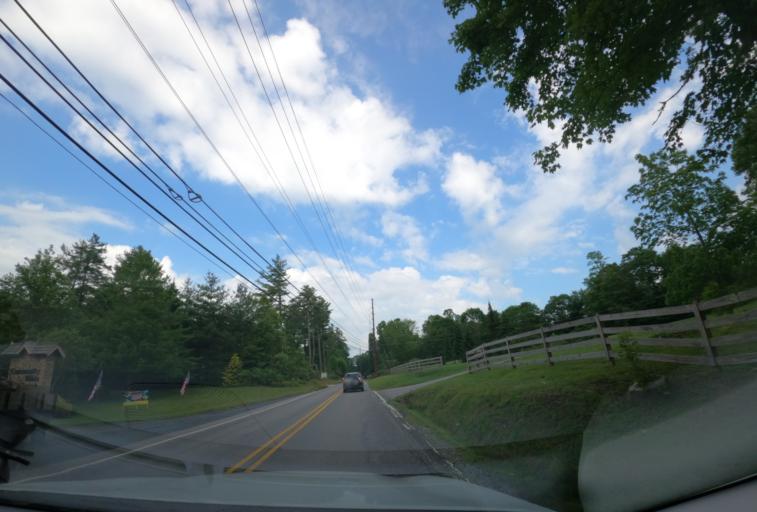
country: US
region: North Carolina
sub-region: Macon County
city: Franklin
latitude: 35.0859
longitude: -83.1789
